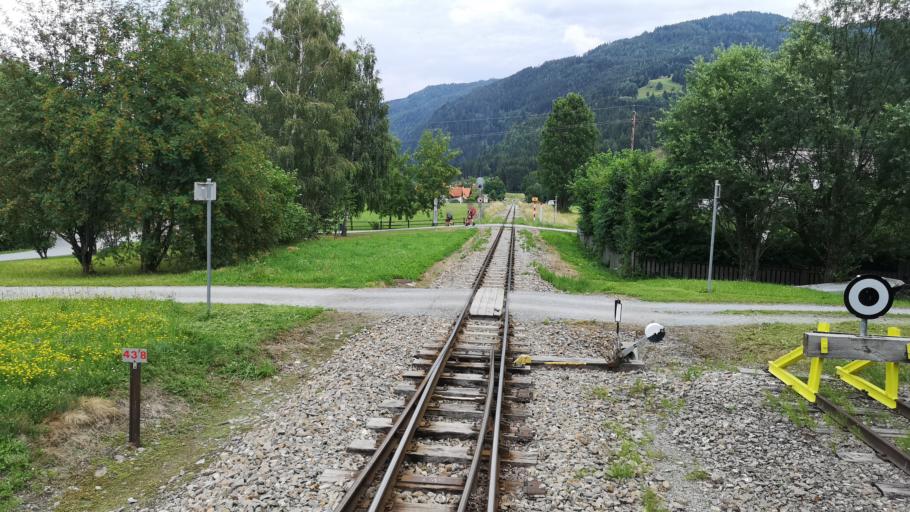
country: AT
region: Styria
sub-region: Politischer Bezirk Murau
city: Stadl an der Mur
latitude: 47.0852
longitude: 13.9834
